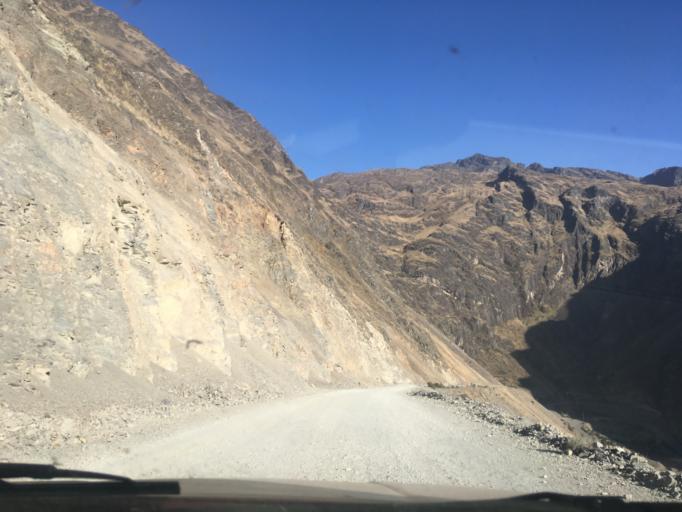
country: BO
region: La Paz
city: Quime
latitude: -17.0056
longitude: -67.2742
